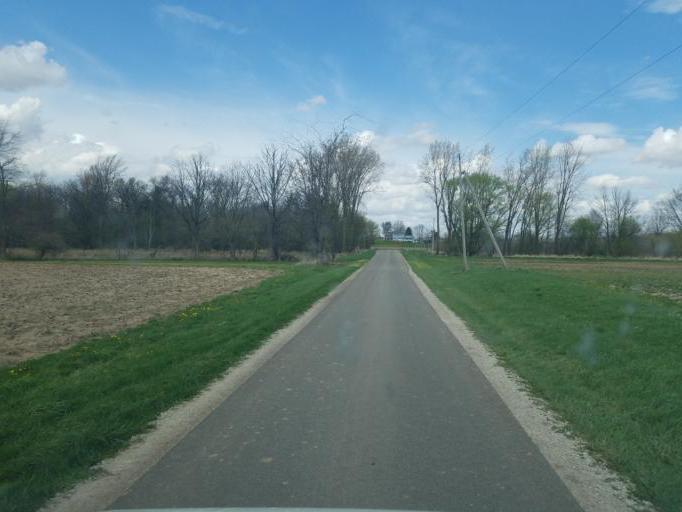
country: US
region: Ohio
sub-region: Crawford County
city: Bucyrus
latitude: 40.8987
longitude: -82.9881
